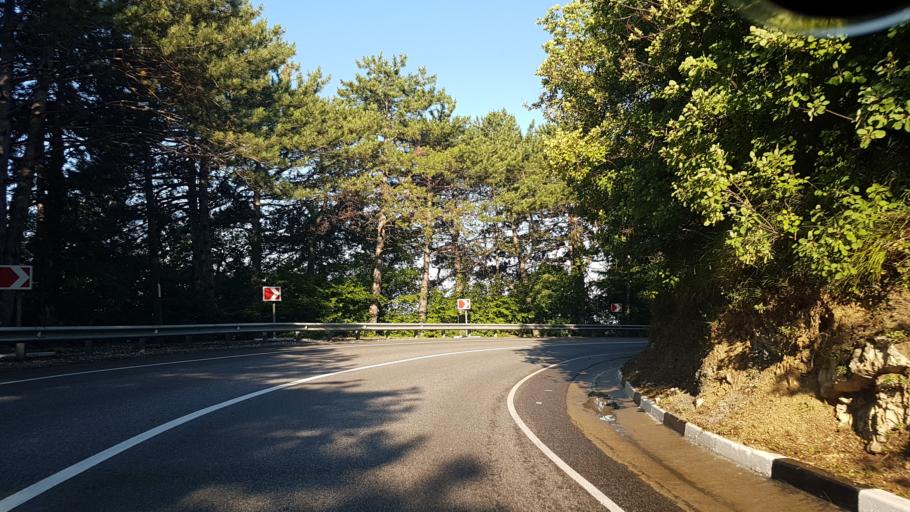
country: RU
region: Krasnodarskiy
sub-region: Sochi City
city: Lazarevskoye
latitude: 43.8218
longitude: 39.4370
